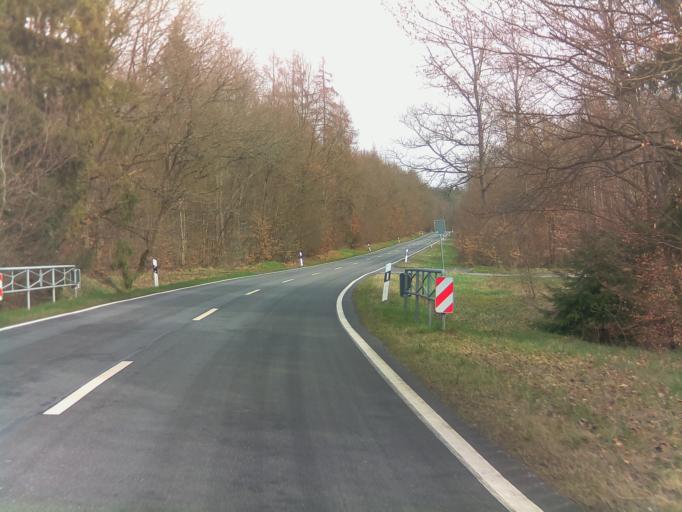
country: DE
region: Rheinland-Pfalz
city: Gebroth
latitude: 49.8906
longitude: 7.6636
